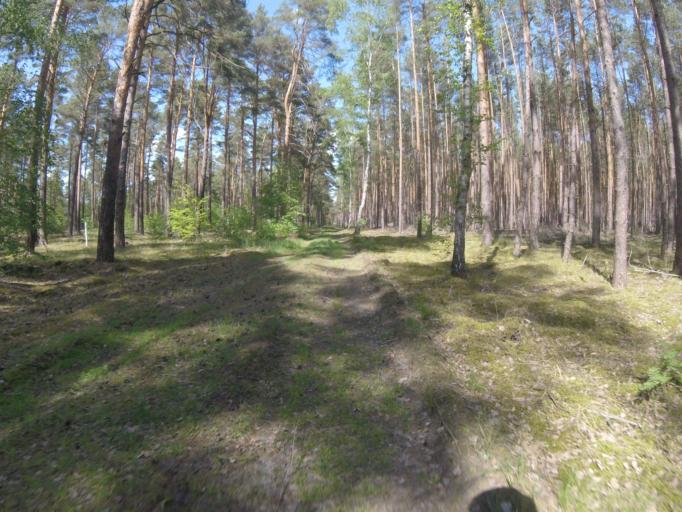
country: DE
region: Brandenburg
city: Schwerin
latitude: 52.1548
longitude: 13.6052
